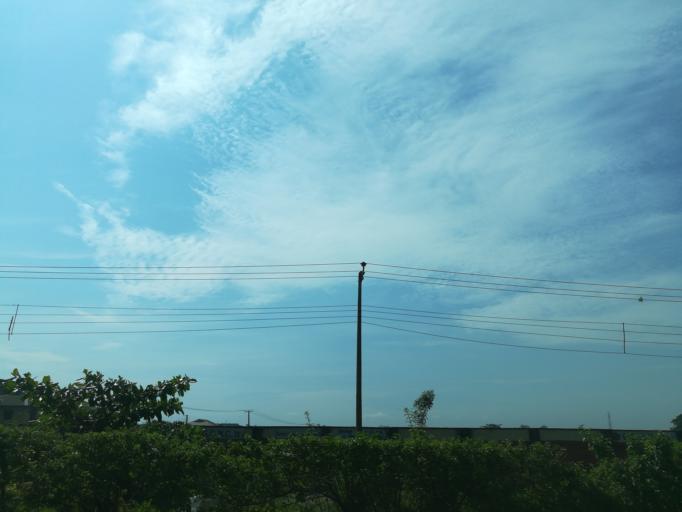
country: NG
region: Lagos
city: Ebute Ikorodu
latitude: 6.6210
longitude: 3.4809
